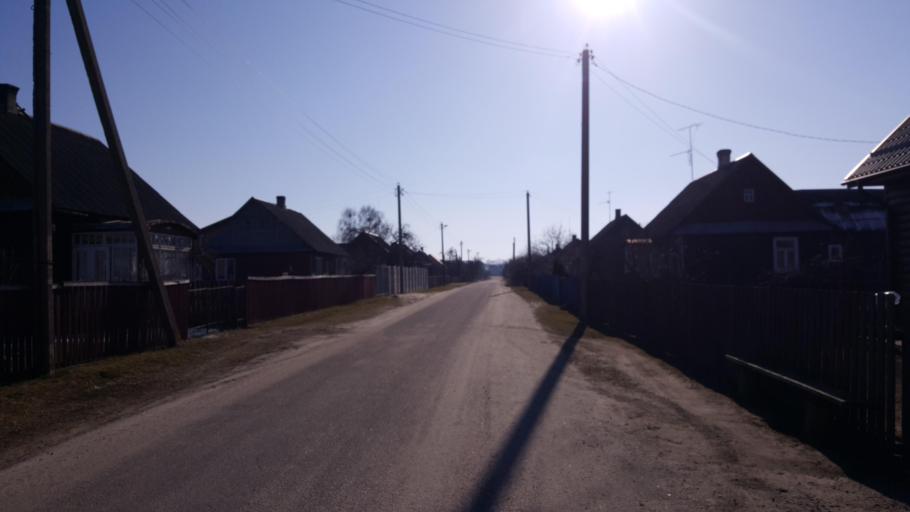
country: BY
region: Brest
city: Kamyanyets
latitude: 52.3987
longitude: 23.8155
